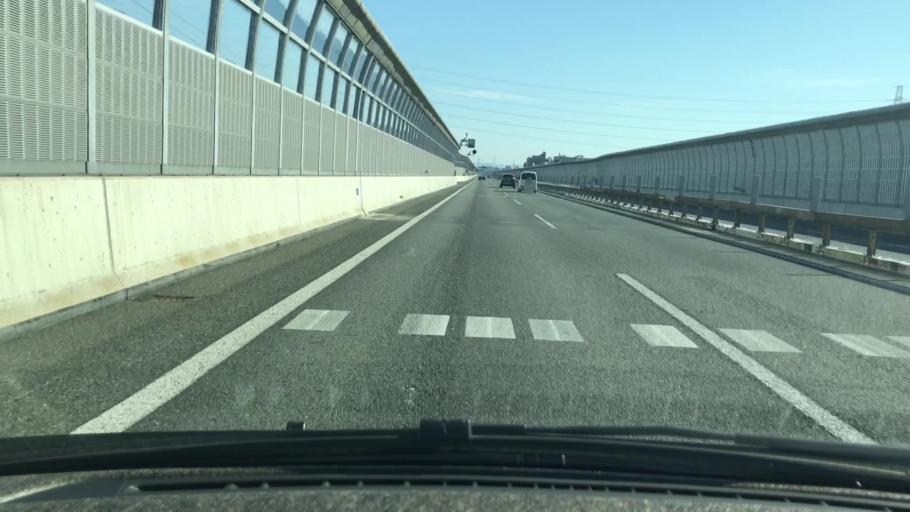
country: JP
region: Hyogo
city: Amagasaki
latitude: 34.7442
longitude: 135.3841
